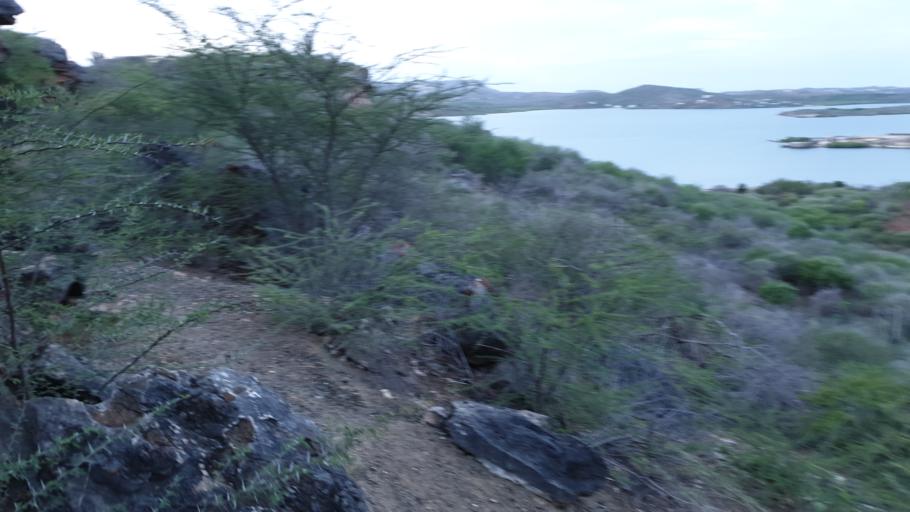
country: CW
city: Newport
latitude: 12.1288
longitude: -68.8140
